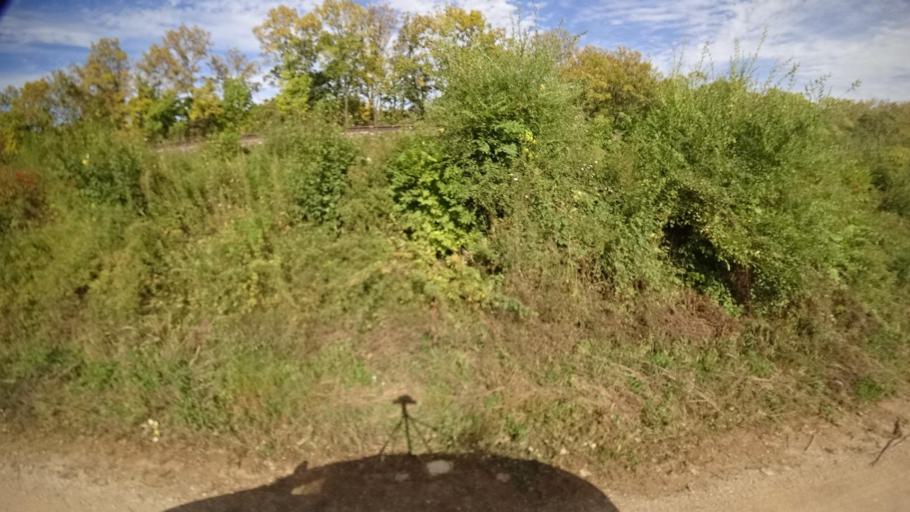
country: RU
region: Primorskiy
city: Yakovlevka
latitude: 44.3917
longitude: 133.6087
